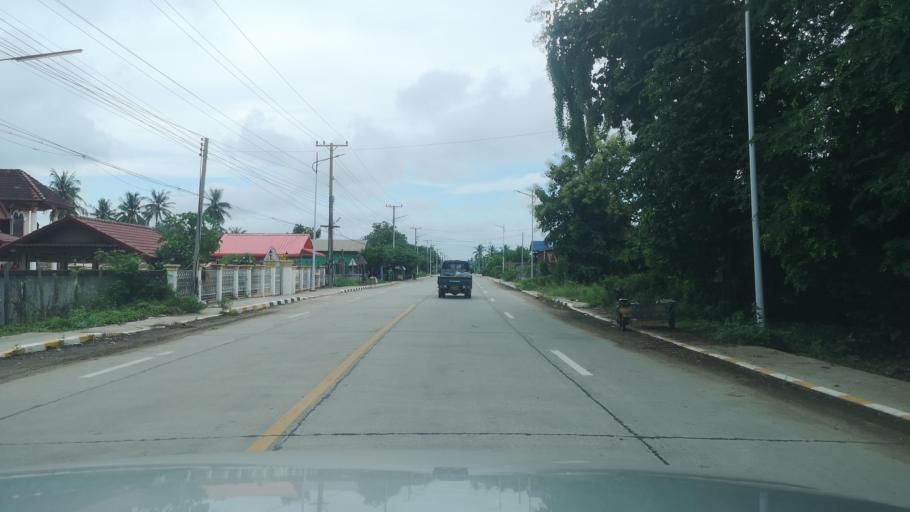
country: TH
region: Nong Khai
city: Tha Bo
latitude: 17.8250
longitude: 102.6588
